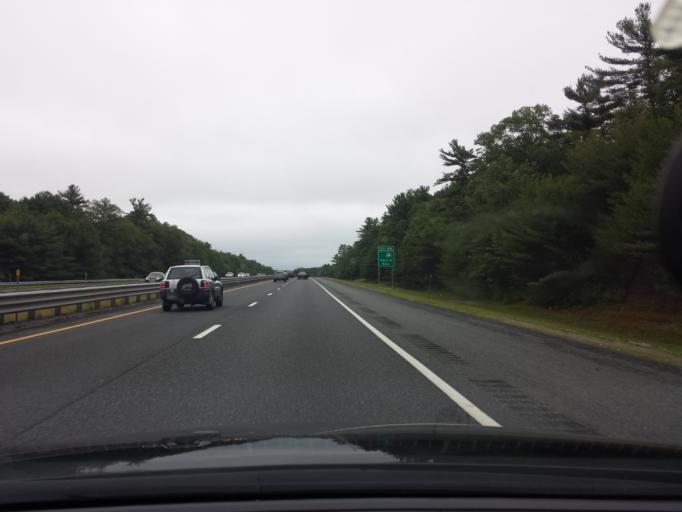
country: US
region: Rhode Island
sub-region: Kent County
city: West Greenwich
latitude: 41.6502
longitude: -71.5984
